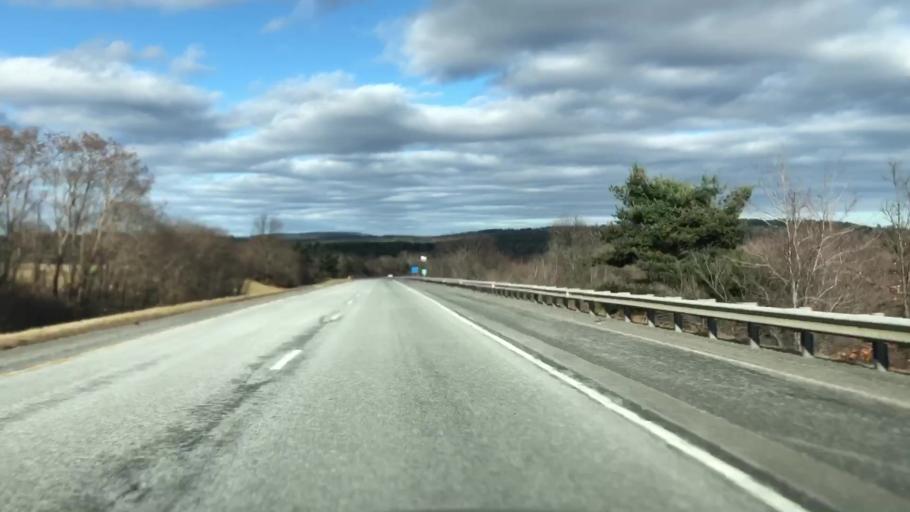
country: US
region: Massachusetts
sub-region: Worcester County
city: Sterling
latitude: 42.4100
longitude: -71.7946
